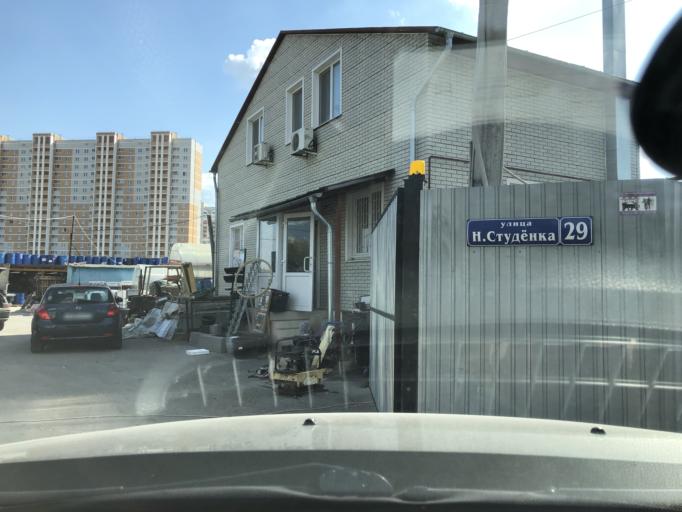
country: RU
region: Tula
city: Tula
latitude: 54.2063
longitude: 37.5731
